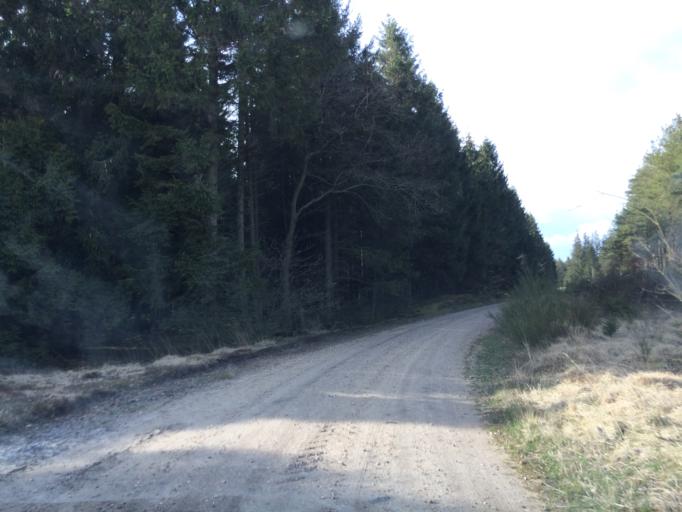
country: DK
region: Central Jutland
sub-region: Holstebro Kommune
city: Ulfborg
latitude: 56.2284
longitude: 8.4921
